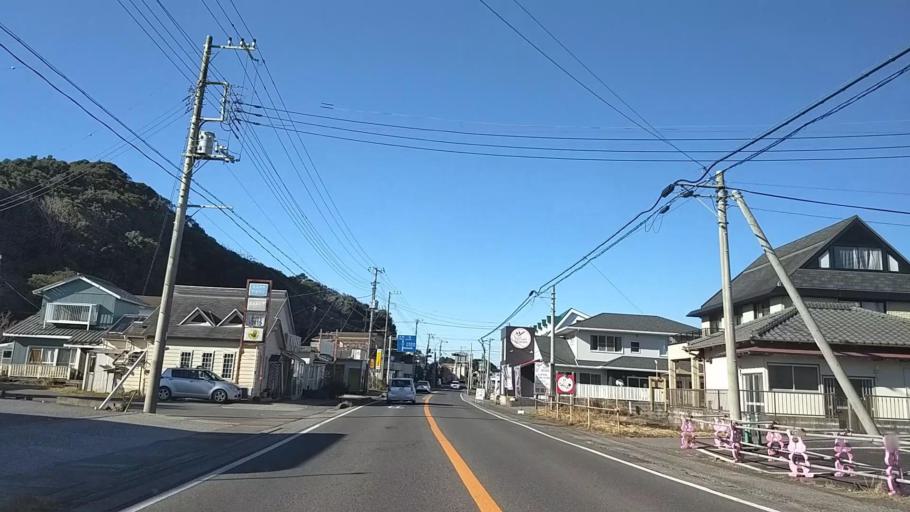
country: JP
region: Chiba
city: Ohara
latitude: 35.3259
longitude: 140.3995
